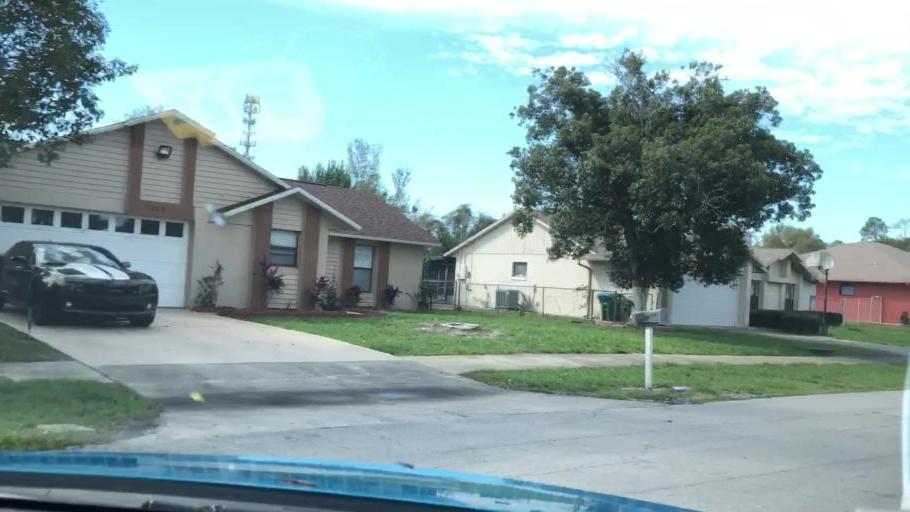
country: US
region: Florida
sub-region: Volusia County
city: Deltona
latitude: 28.8765
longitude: -81.2336
